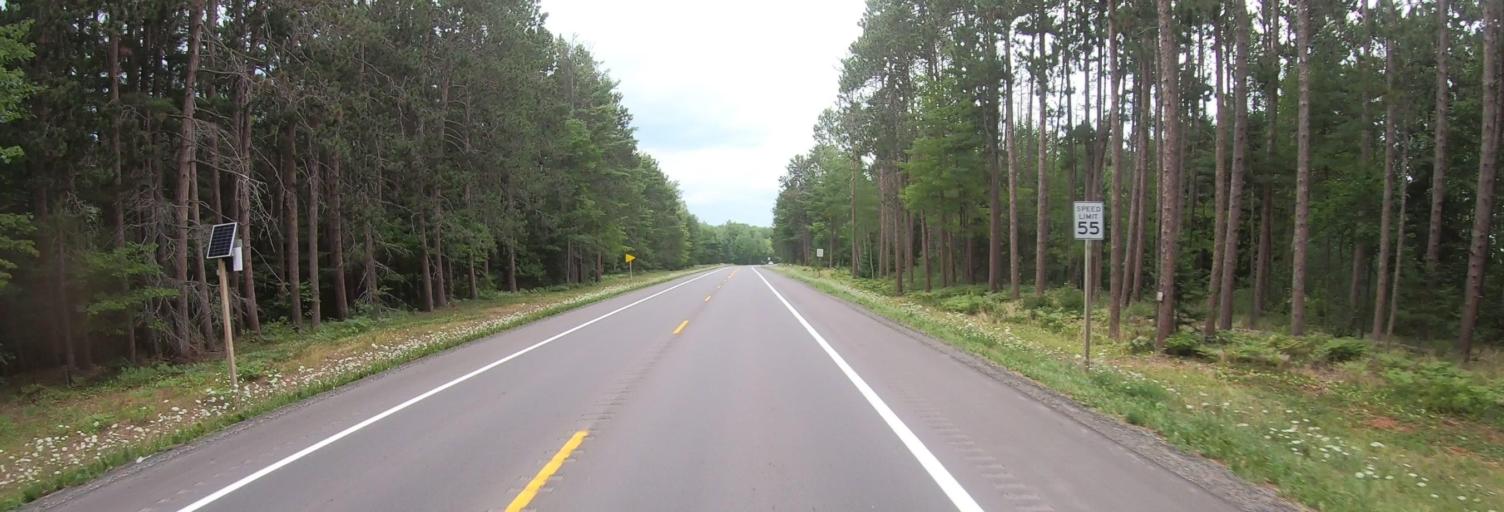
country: US
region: Michigan
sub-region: Baraga County
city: Baraga
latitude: 46.7991
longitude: -88.4745
